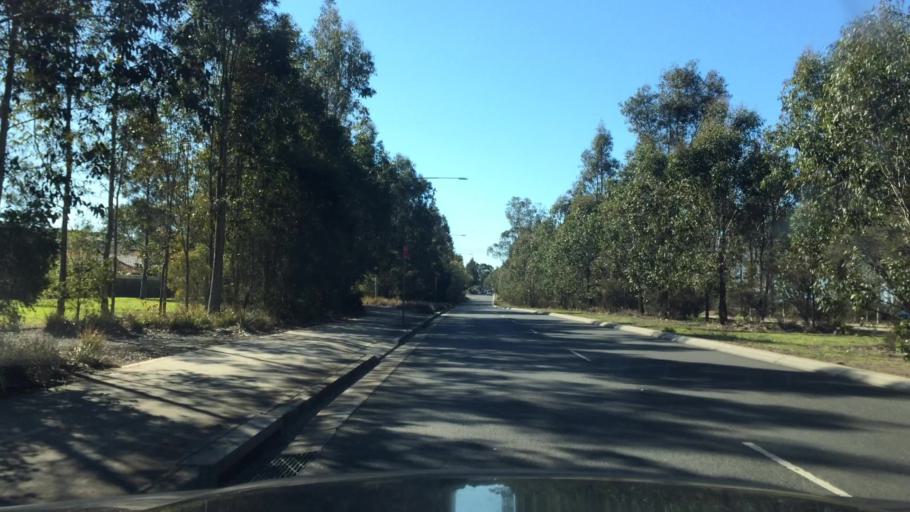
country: AU
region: New South Wales
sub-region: Liverpool
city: Miller
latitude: -33.9345
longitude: 150.8439
